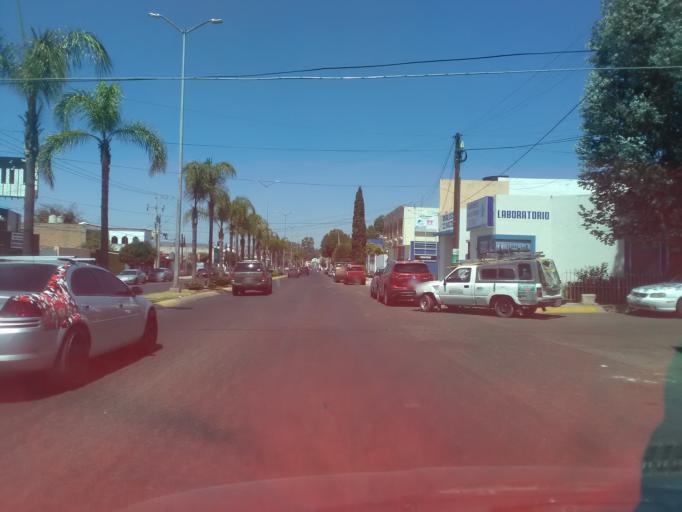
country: MX
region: Durango
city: Victoria de Durango
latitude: 24.0141
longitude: -104.6783
